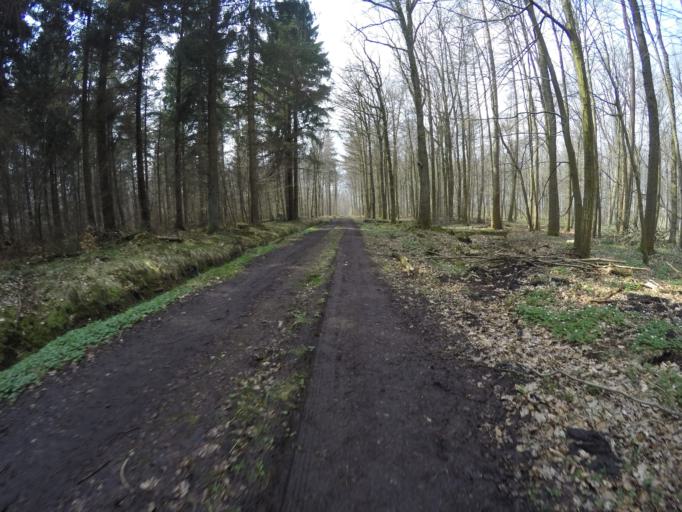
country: DE
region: Schleswig-Holstein
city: Borstel-Hohenraden
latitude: 53.7225
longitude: 9.8084
